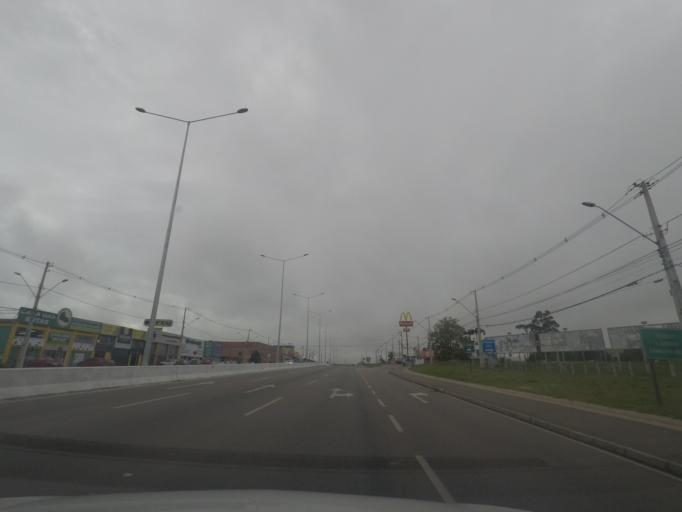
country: BR
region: Parana
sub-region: Pinhais
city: Pinhais
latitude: -25.4331
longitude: -49.1878
